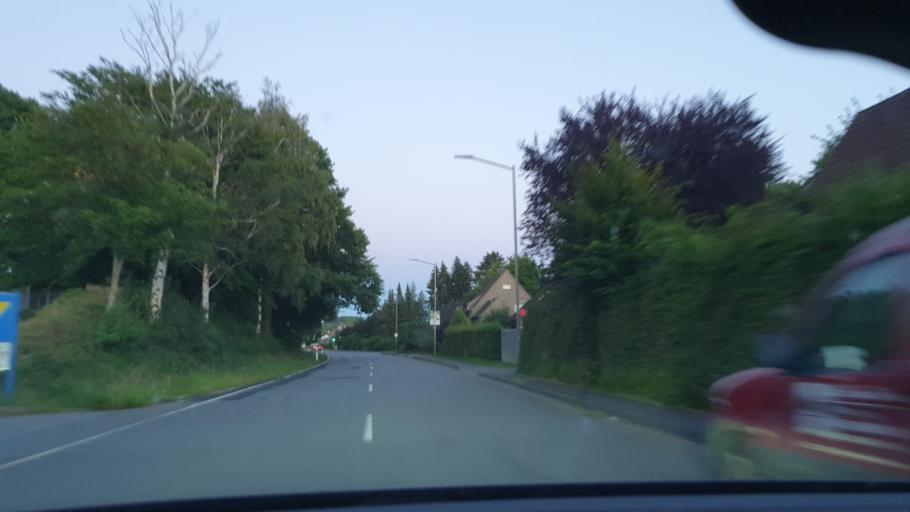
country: DE
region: North Rhine-Westphalia
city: Spenge
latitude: 52.1437
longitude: 8.4906
